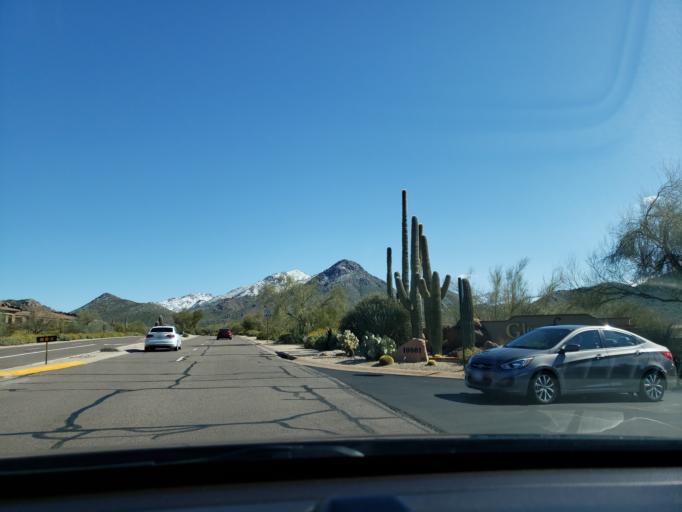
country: US
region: Arizona
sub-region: Maricopa County
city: Carefree
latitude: 33.7089
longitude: -111.8489
